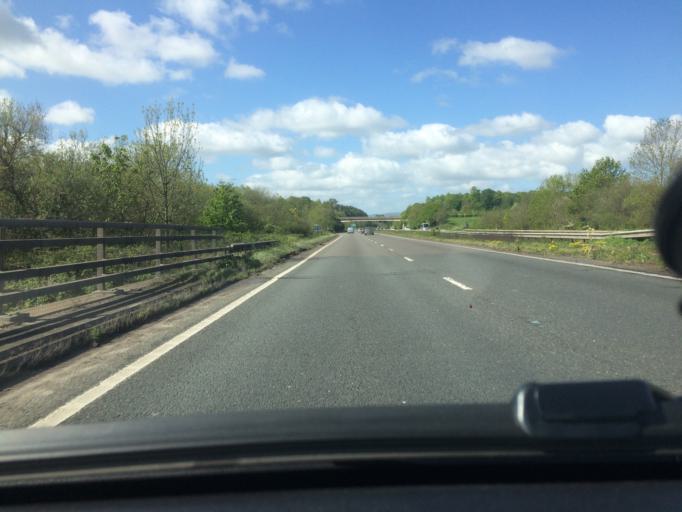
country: GB
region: England
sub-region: Cheshire West and Chester
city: Eccleston
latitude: 53.1632
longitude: -2.8769
